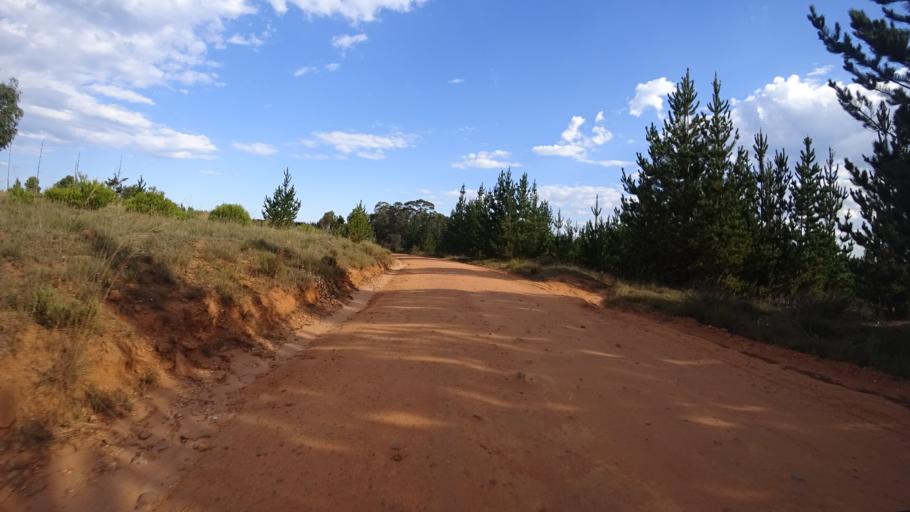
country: AU
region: New South Wales
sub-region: Lithgow
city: Lithgow
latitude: -33.3544
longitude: 150.2527
